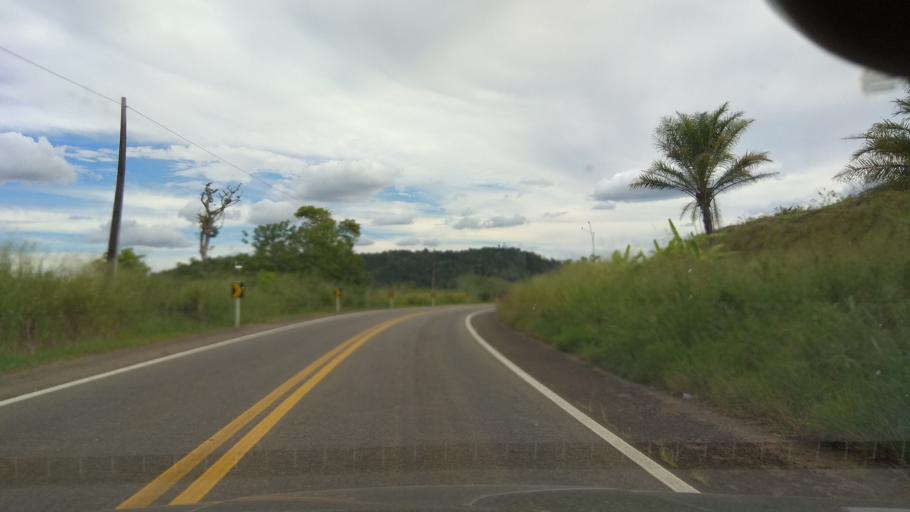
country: BR
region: Bahia
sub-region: Ubata
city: Ubata
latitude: -14.2101
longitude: -39.5782
